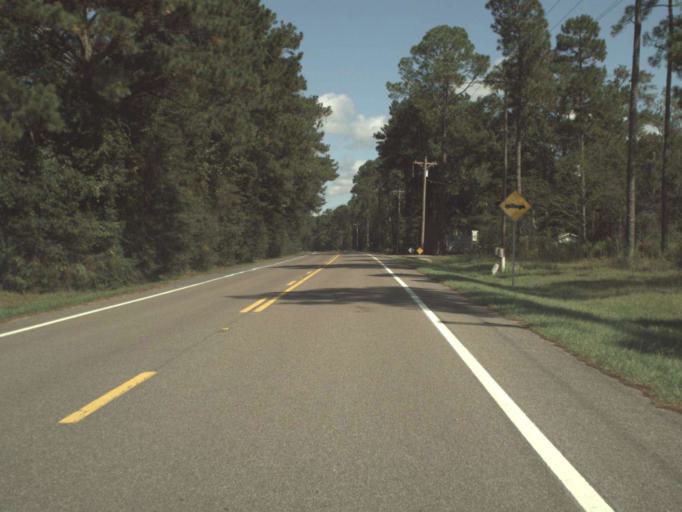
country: US
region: Florida
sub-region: Walton County
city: DeFuniak Springs
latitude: 30.8533
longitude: -86.1157
